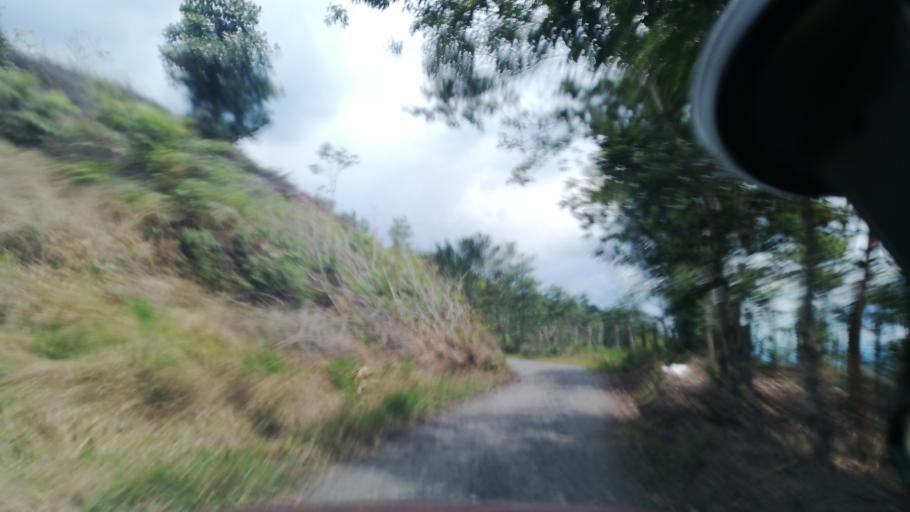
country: CO
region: Cundinamarca
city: Vergara
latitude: 5.2072
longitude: -74.2799
